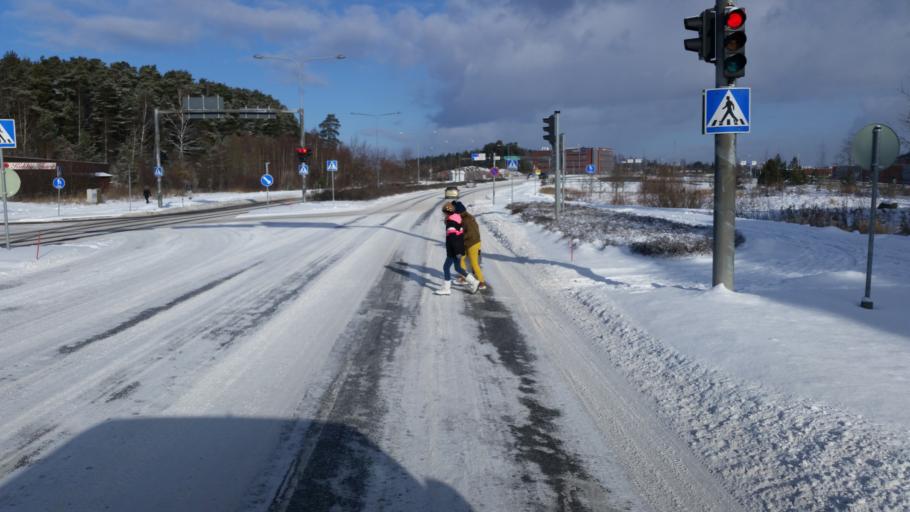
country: FI
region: Varsinais-Suomi
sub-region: Turku
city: Turku
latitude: 60.4343
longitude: 22.3178
